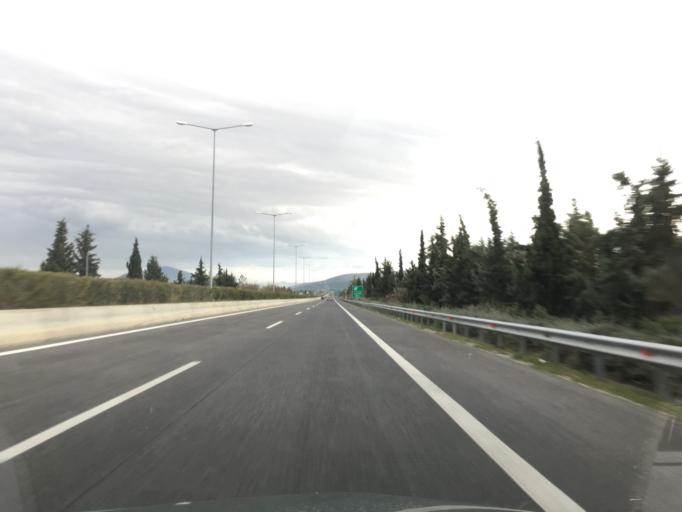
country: GR
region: Thessaly
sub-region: Nomos Magnisias
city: Almyros
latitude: 39.2050
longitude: 22.7582
